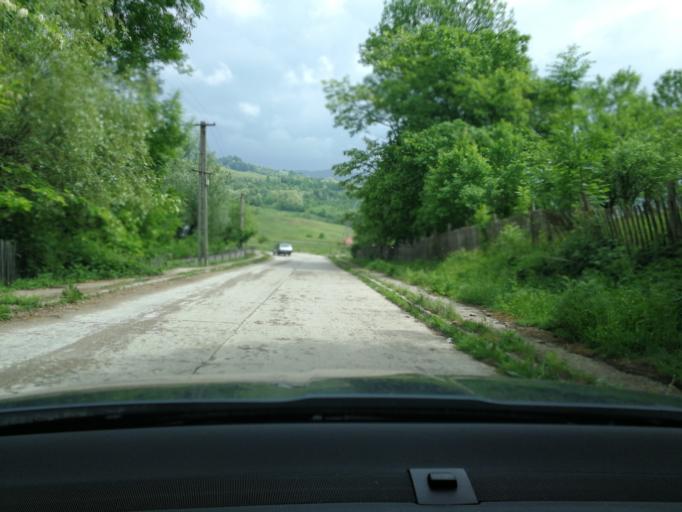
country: RO
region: Prahova
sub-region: Comuna Brebu
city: Pietriceaua
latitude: 45.2068
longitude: 25.8119
